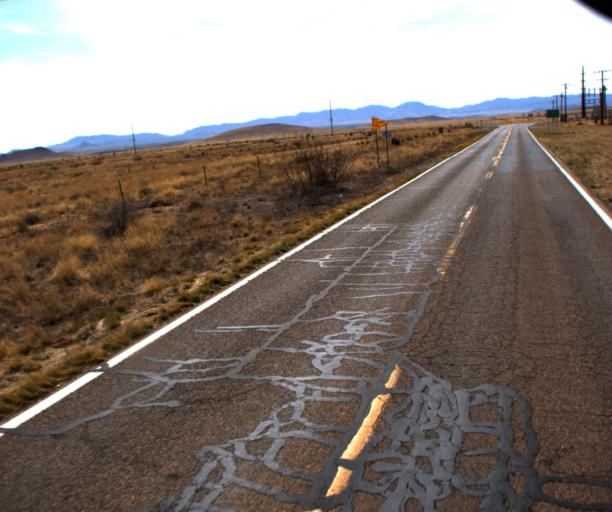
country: US
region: Arizona
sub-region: Cochise County
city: Willcox
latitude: 31.8837
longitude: -109.6924
